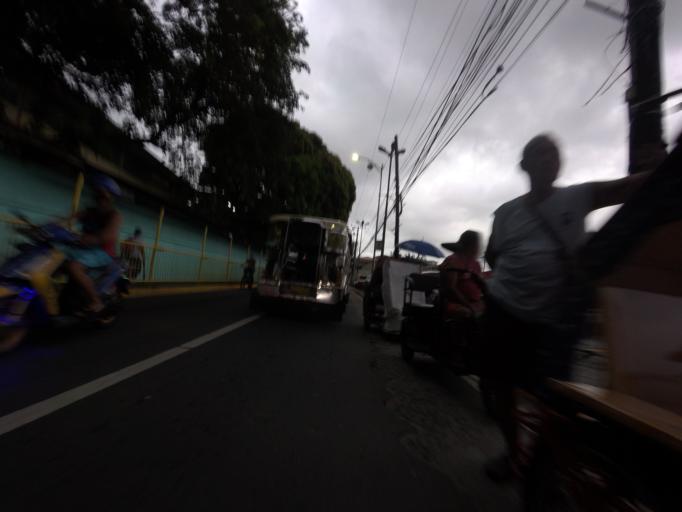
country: PH
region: Metro Manila
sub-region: San Juan
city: San Juan
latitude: 14.5875
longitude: 121.0186
